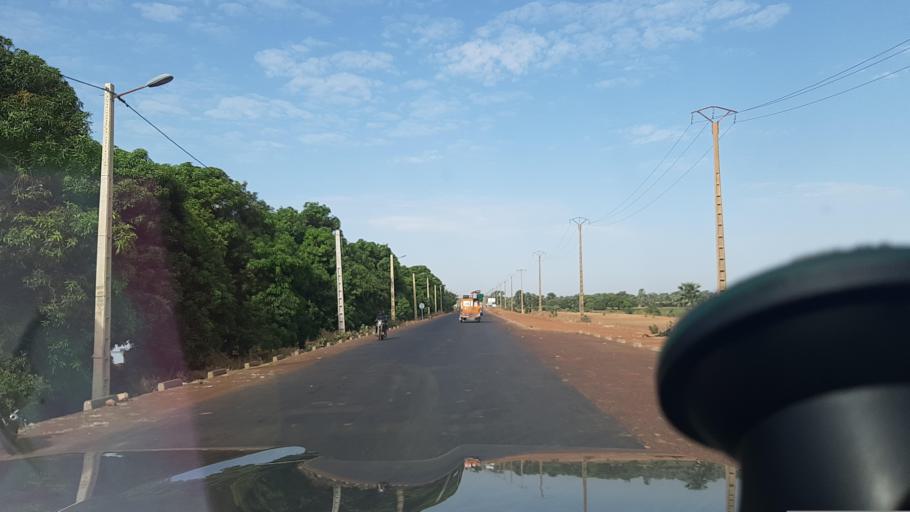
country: ML
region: Segou
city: Markala
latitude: 13.6817
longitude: -6.0858
